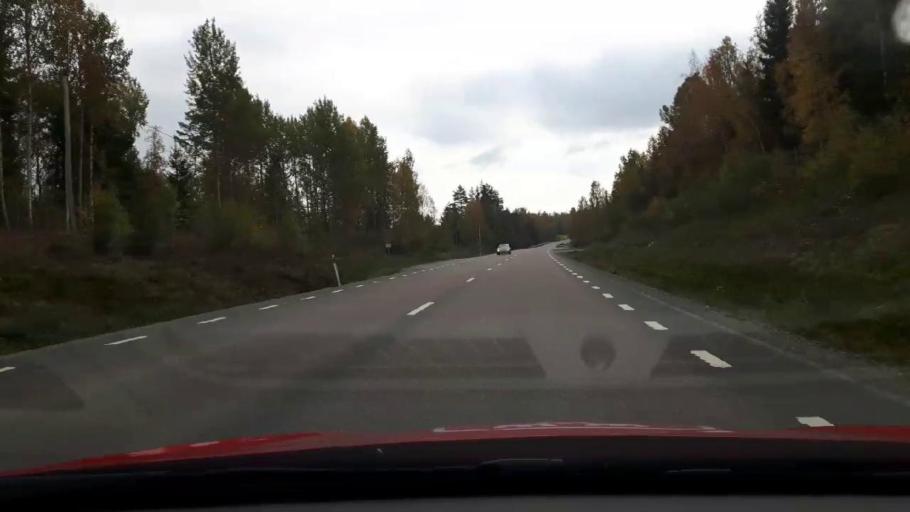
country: SE
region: Gaevleborg
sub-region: Bollnas Kommun
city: Kilafors
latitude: 61.2869
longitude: 16.5123
